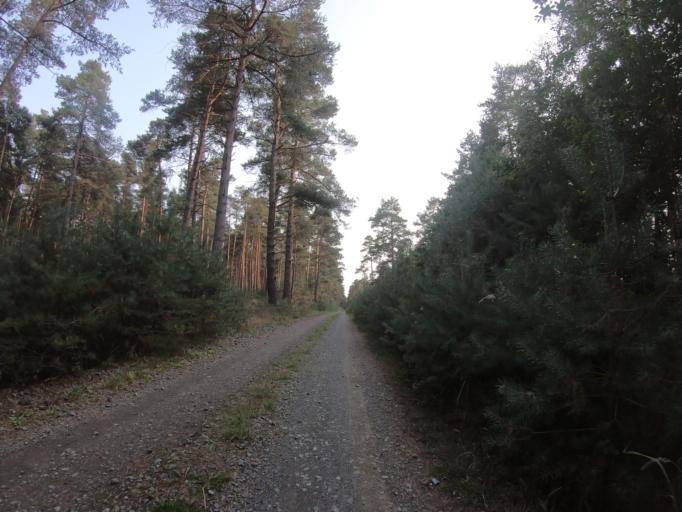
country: DE
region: Lower Saxony
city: Leiferde
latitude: 52.4645
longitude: 10.4498
